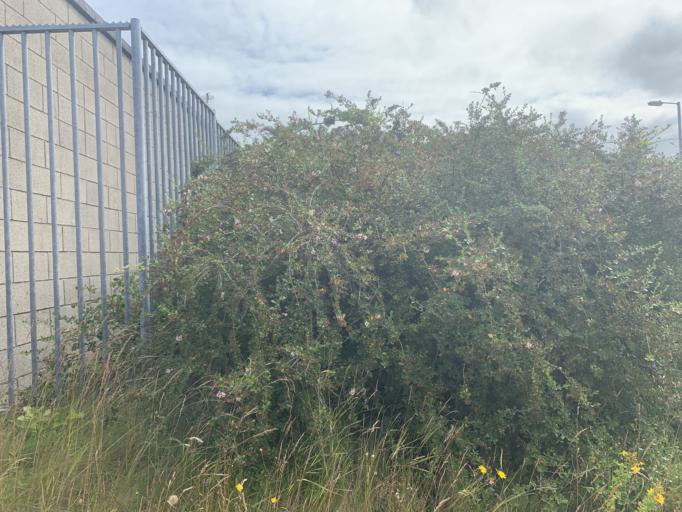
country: GB
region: Scotland
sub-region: Renfrewshire
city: Inchinnan
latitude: 55.8673
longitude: -4.4232
